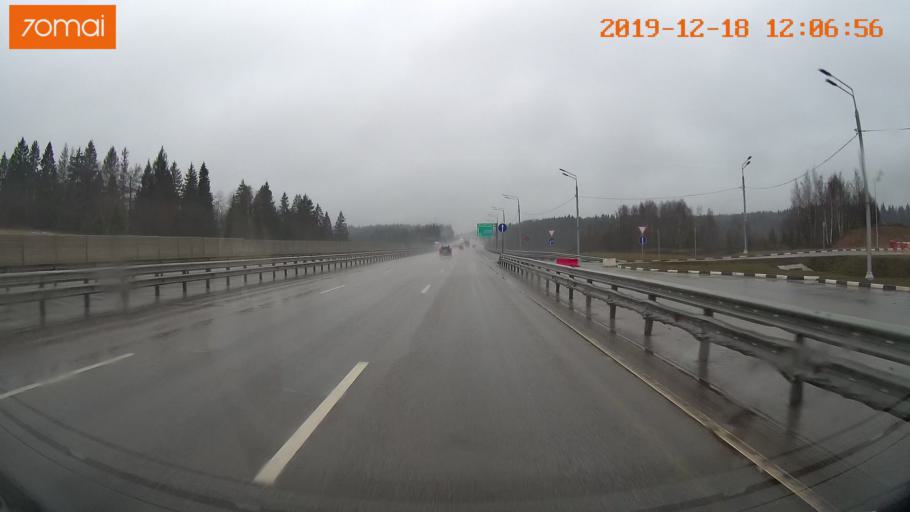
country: RU
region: Moskovskaya
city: Kostrovo
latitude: 55.8856
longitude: 36.6623
